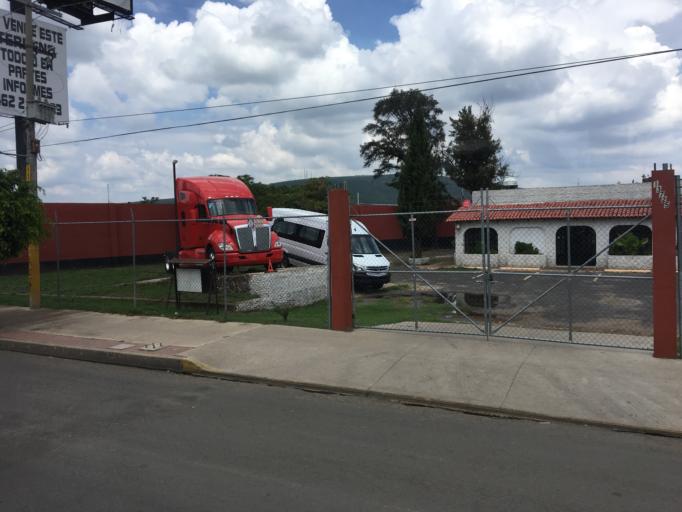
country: MX
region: Guanajuato
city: Irapuato
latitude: 20.7095
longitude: -101.3523
